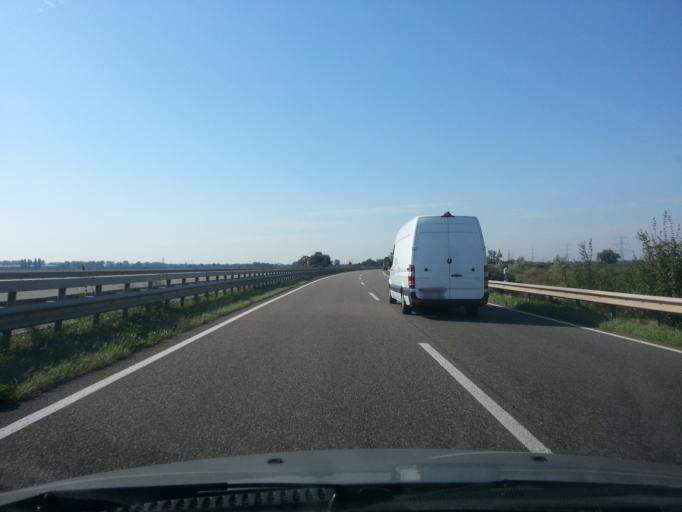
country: DE
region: Rheinland-Pfalz
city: Bobenheim-Roxheim
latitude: 49.5846
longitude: 8.4051
